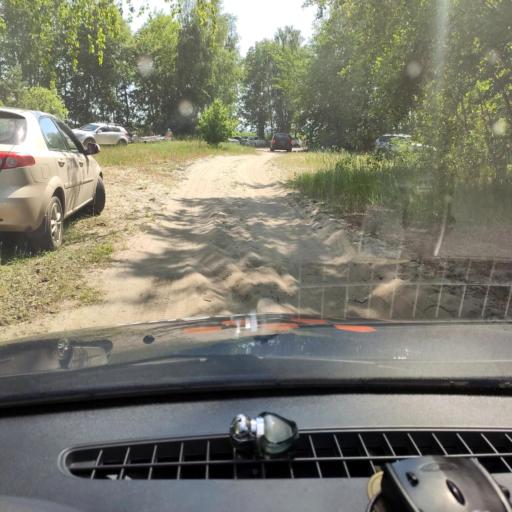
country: RU
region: Voronezj
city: Somovo
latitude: 51.7850
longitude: 39.2857
